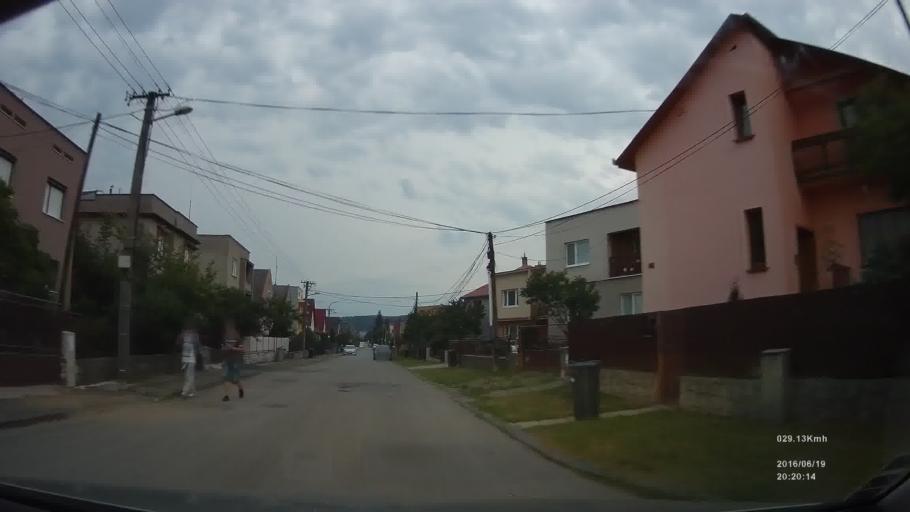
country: SK
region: Presovsky
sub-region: Okres Presov
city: Presov
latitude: 48.9752
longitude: 21.2593
